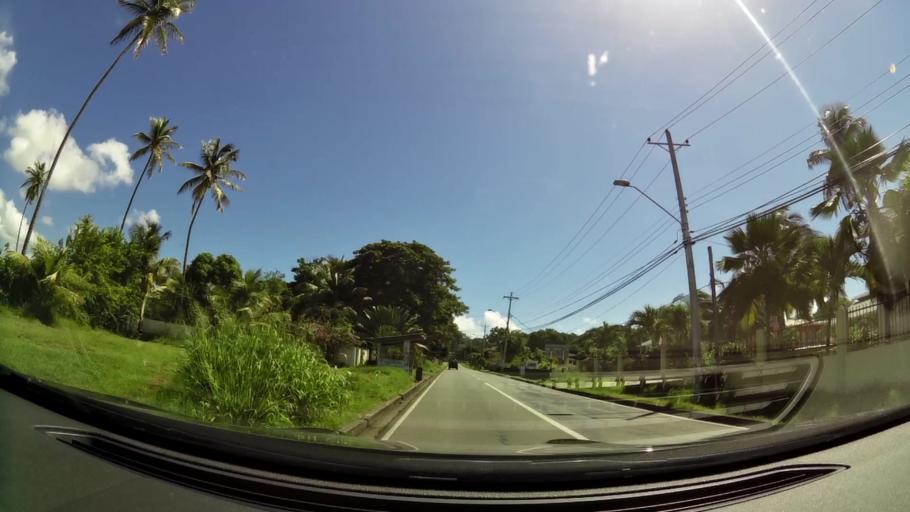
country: TT
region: Tobago
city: Scarborough
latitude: 11.1816
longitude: -60.8002
